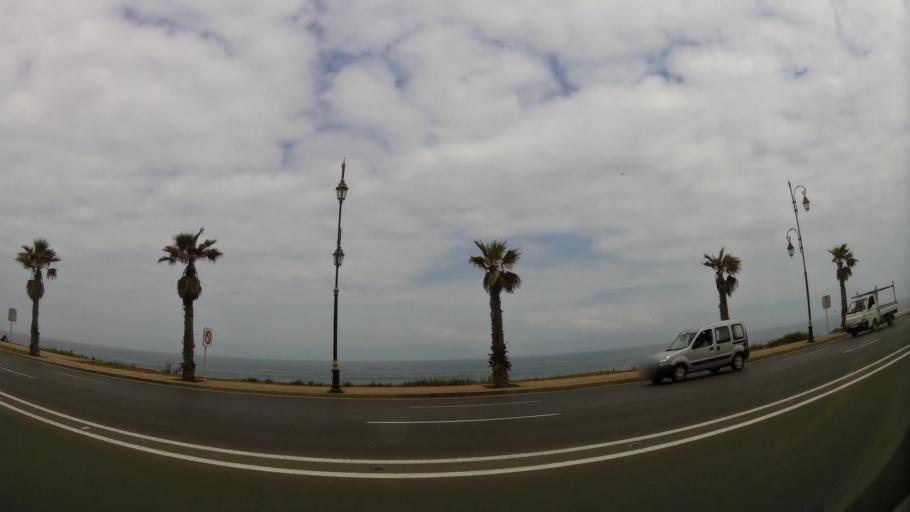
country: MA
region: Rabat-Sale-Zemmour-Zaer
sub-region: Rabat
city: Rabat
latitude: 34.0019
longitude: -6.8734
